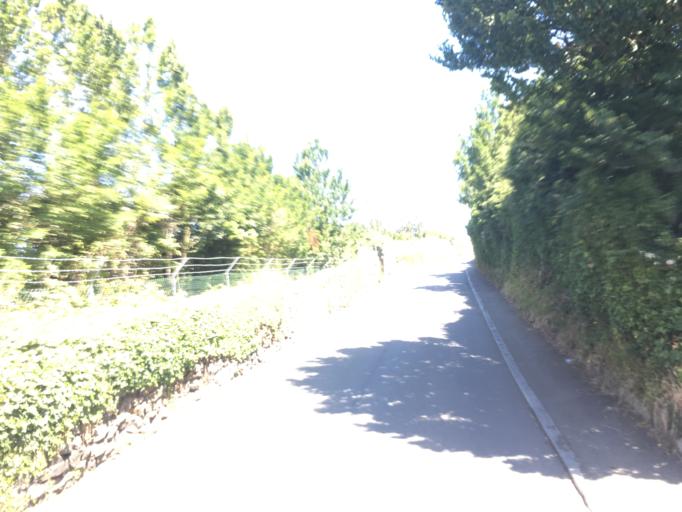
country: GG
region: St Peter Port
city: Saint Peter Port
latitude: 49.4879
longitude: -2.5155
